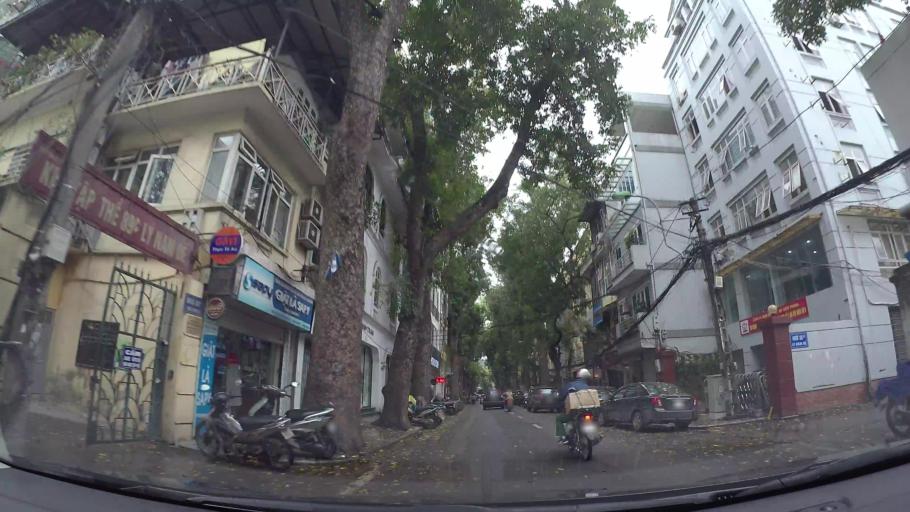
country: VN
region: Ha Noi
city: Hoan Kiem
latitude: 21.0320
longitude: 105.8443
